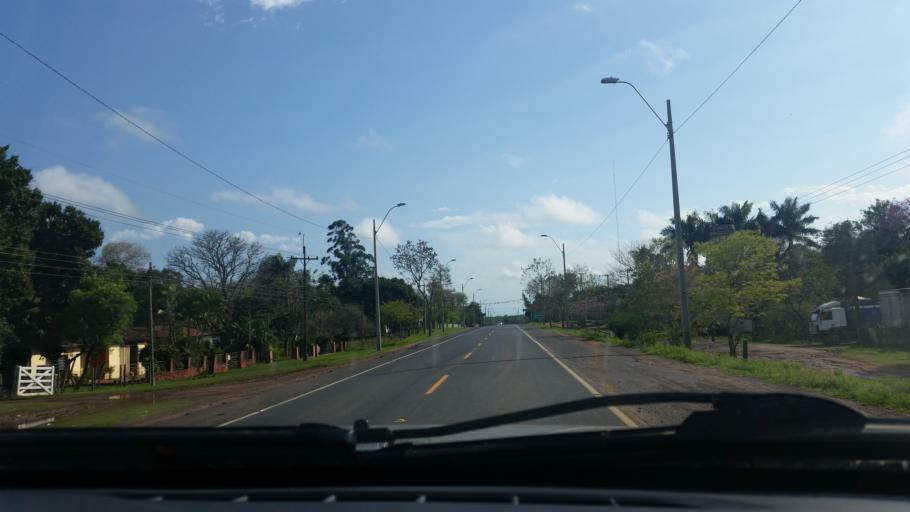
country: PY
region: Presidente Hayes
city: Benjamin Aceval
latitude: -24.9658
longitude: -57.5488
